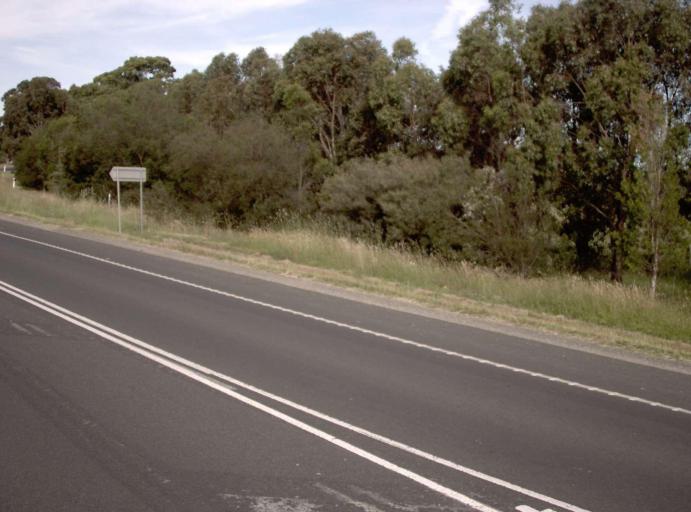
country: AU
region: Victoria
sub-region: Latrobe
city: Traralgon
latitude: -38.1296
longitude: 146.5625
